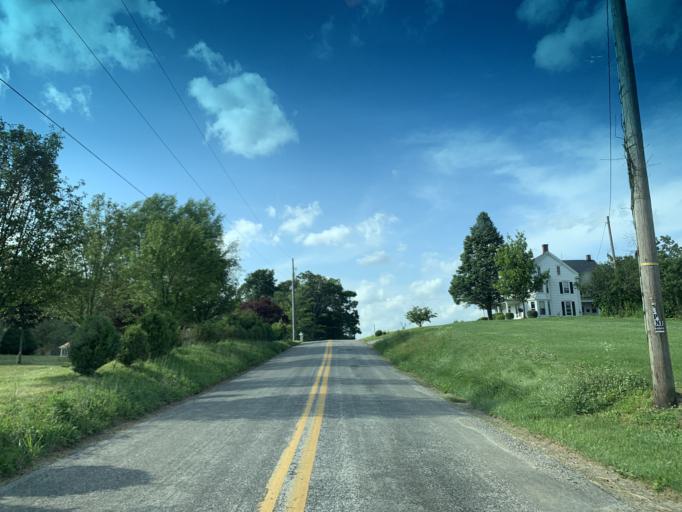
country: US
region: Pennsylvania
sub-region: York County
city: Stewartstown
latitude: 39.7381
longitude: -76.5428
